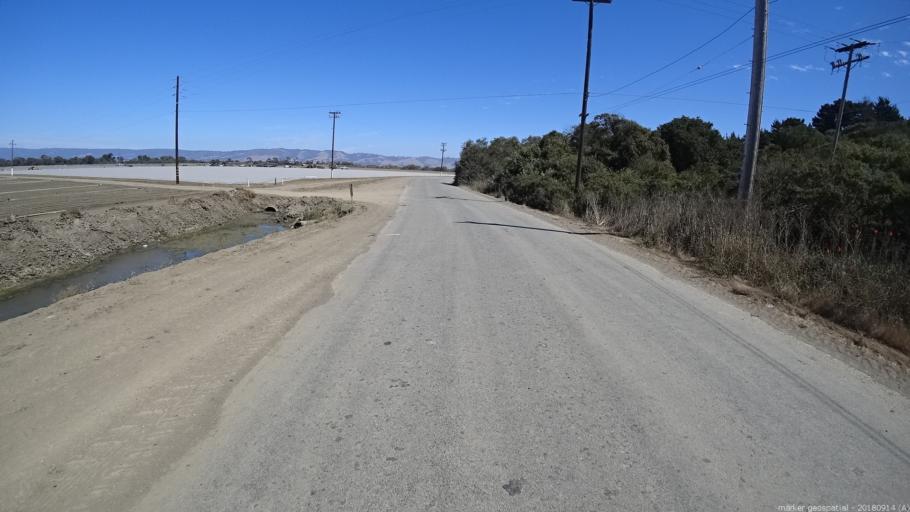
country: US
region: California
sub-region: Santa Cruz County
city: Watsonville
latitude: 36.8751
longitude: -121.7779
